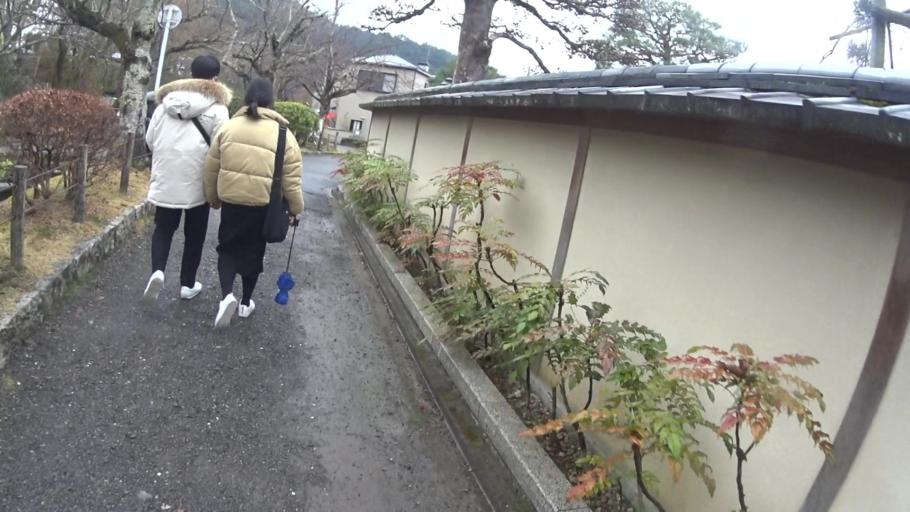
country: JP
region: Kyoto
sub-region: Kyoto-shi
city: Kamigyo-ku
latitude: 35.0190
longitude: 135.7944
